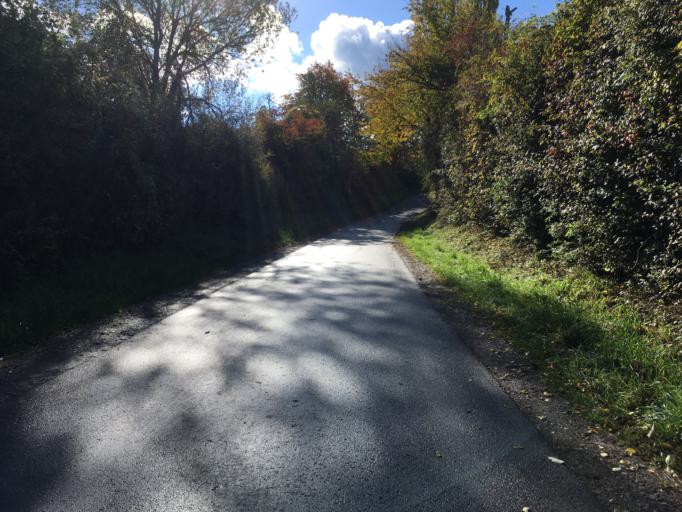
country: DE
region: Baden-Wuerttemberg
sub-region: Regierungsbezirk Stuttgart
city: Pfedelbach
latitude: 49.1883
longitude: 9.4803
